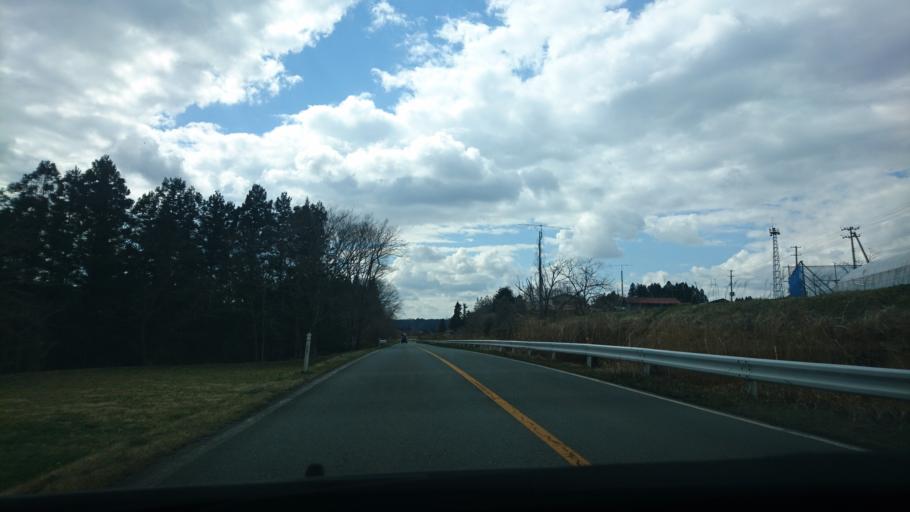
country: JP
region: Iwate
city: Hanamaki
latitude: 39.3624
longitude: 141.2687
